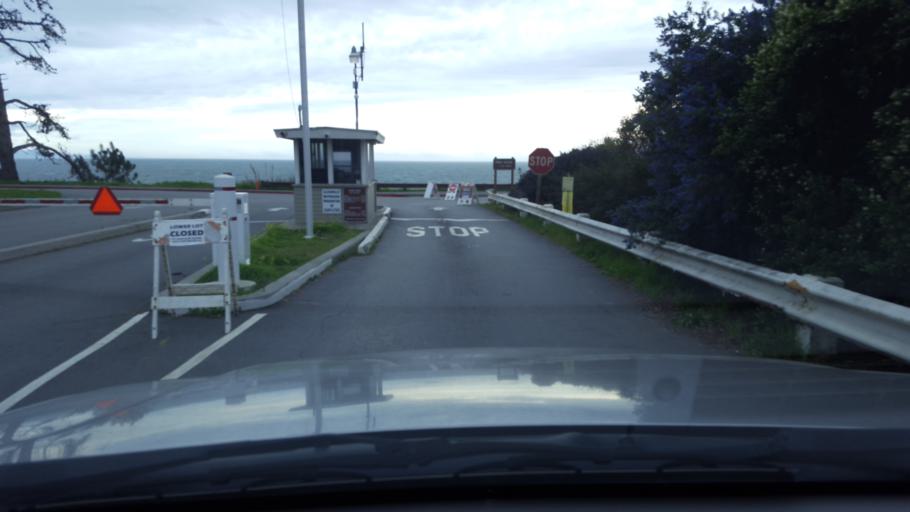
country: US
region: California
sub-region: Santa Cruz County
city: Seacliff
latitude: 36.9729
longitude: -121.9127
